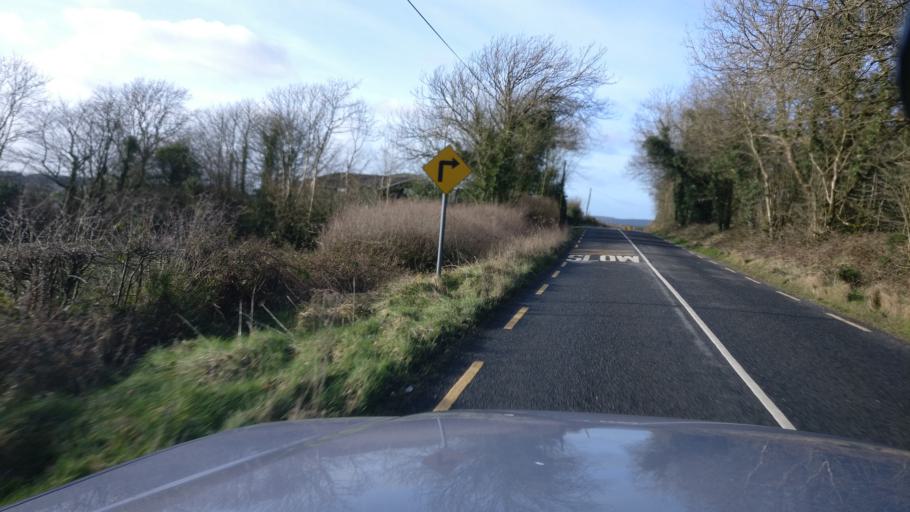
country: IE
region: Leinster
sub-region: Laois
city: Stradbally
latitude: 52.9222
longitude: -7.1915
